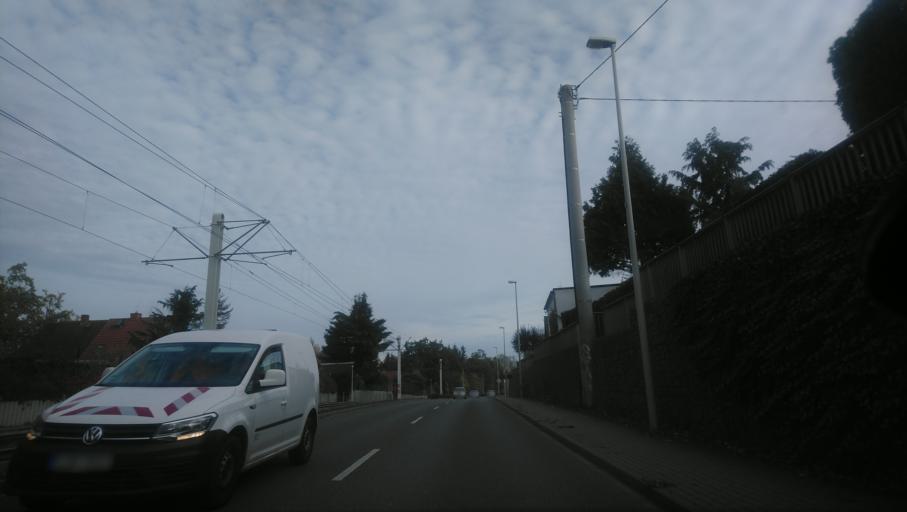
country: DE
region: Saxony
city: Zwickau
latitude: 50.6975
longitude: 12.4812
